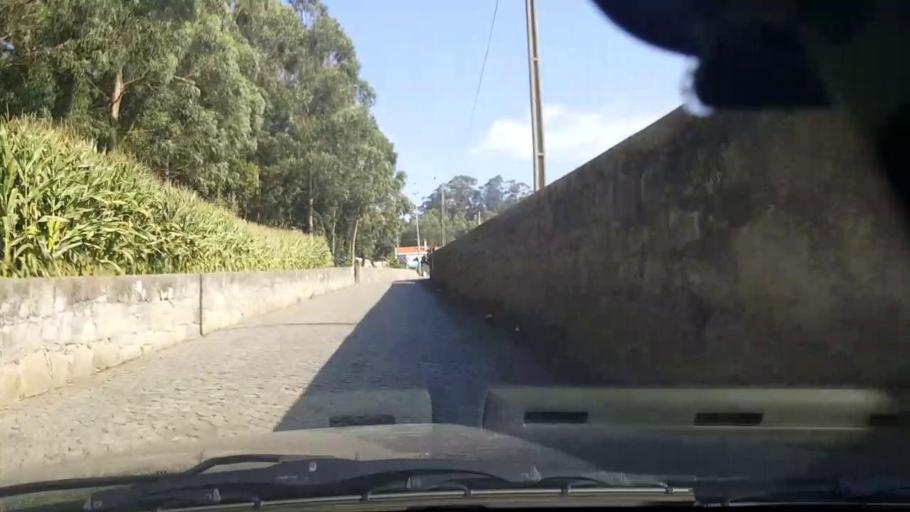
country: PT
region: Porto
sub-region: Maia
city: Gemunde
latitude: 41.2742
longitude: -8.6681
